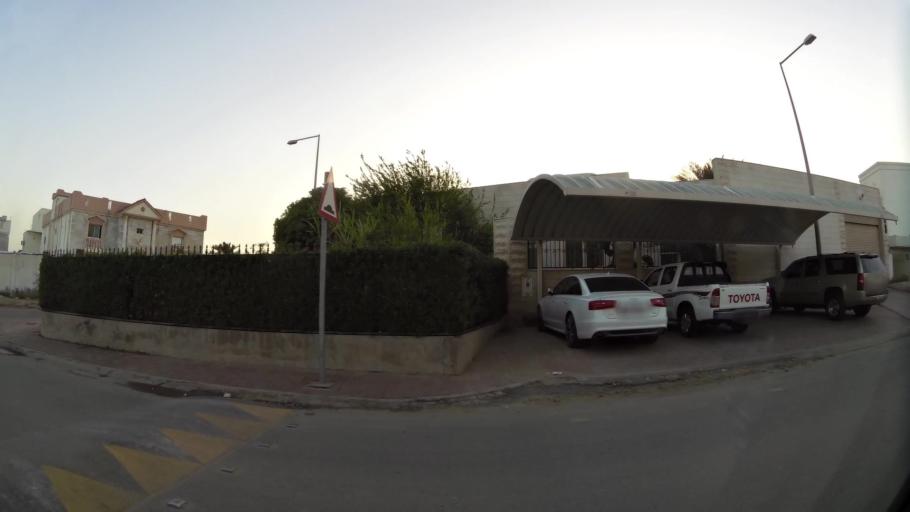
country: QA
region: Baladiyat ar Rayyan
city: Ar Rayyan
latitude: 25.3244
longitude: 51.4638
